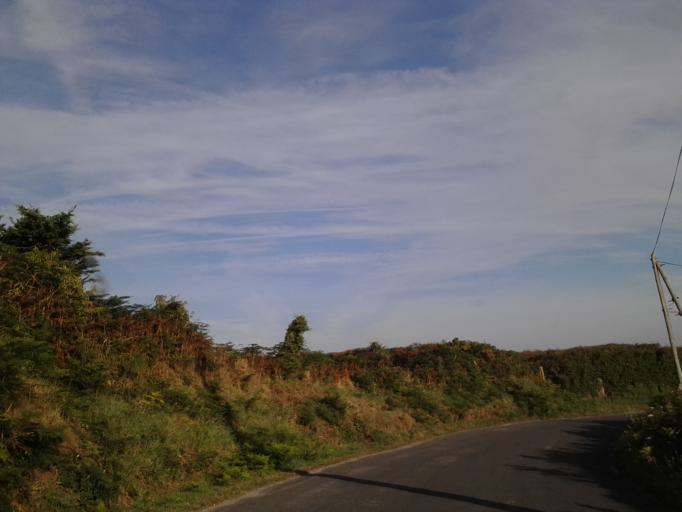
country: FR
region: Lower Normandy
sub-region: Departement de la Manche
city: Fermanville
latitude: 49.6851
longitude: -1.4721
